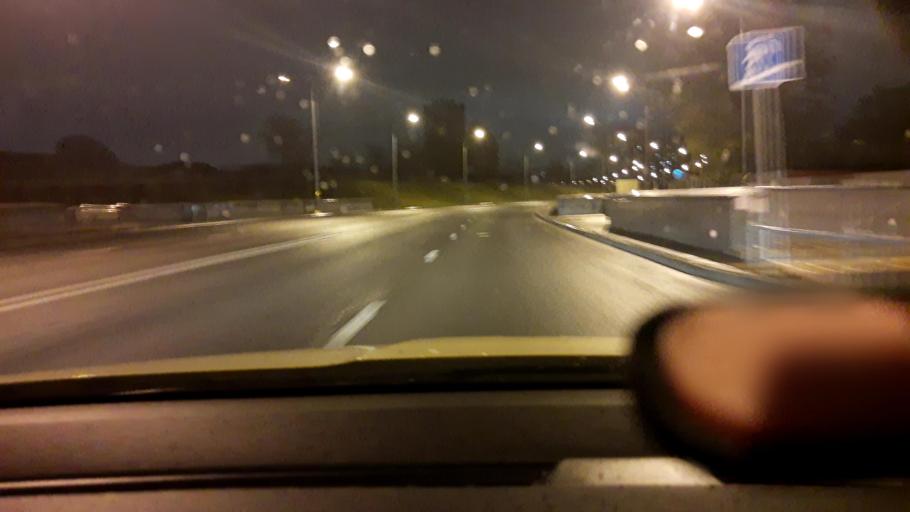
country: RU
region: Moscow
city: Ramenki
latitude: 55.6931
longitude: 37.5130
